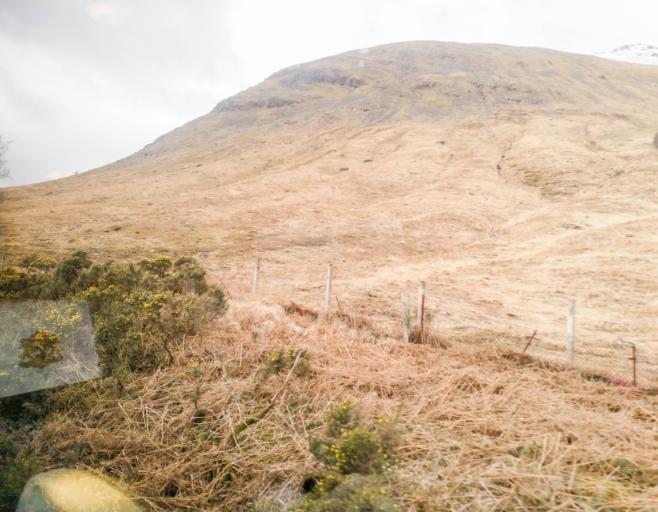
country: GB
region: Scotland
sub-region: Argyll and Bute
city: Garelochhead
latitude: 56.4892
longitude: -4.7093
